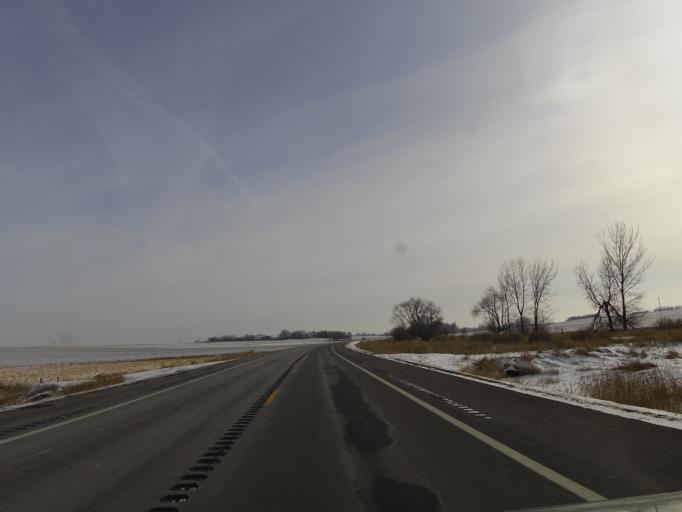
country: US
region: Minnesota
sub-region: McLeod County
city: Hutchinson
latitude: 44.9095
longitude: -94.4460
